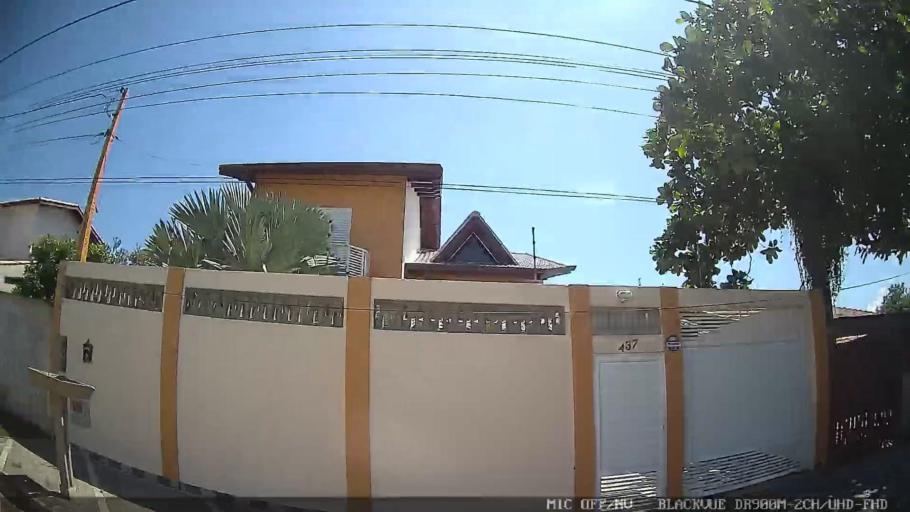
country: BR
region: Sao Paulo
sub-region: Peruibe
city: Peruibe
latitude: -24.2994
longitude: -46.9768
